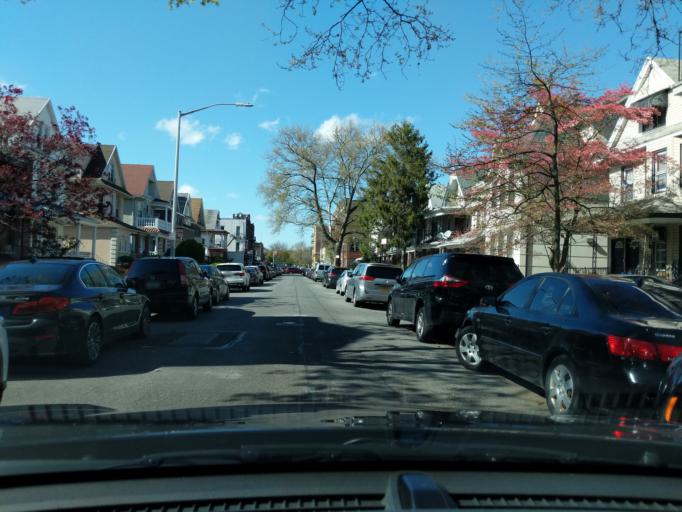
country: US
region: New York
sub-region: Kings County
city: Brooklyn
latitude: 40.6347
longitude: -73.9738
